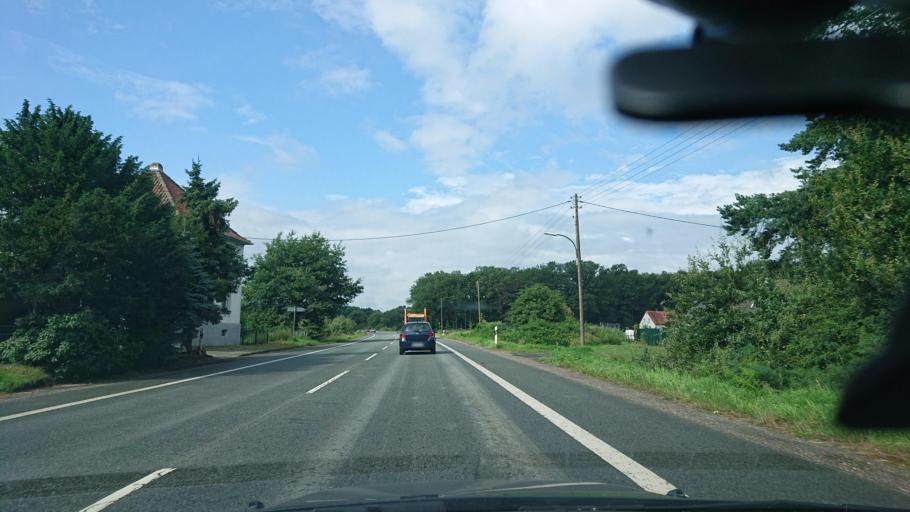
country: DE
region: North Rhine-Westphalia
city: Lunen
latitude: 51.6298
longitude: 7.5813
